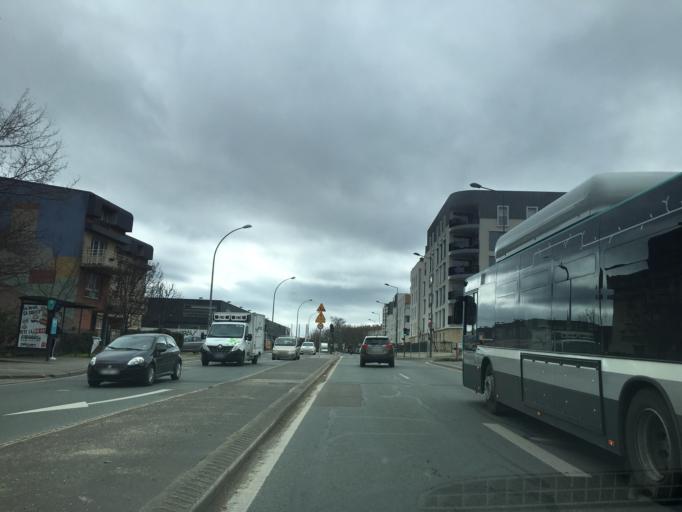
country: FR
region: Ile-de-France
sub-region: Departement du Val-de-Marne
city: Bonneuil-sur-Marne
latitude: 48.7755
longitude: 2.4899
